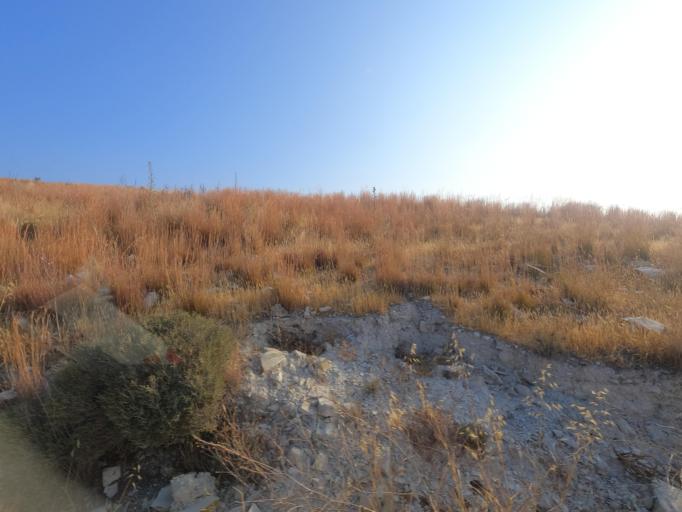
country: CY
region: Larnaka
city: Psevdas
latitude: 34.9178
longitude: 33.5027
